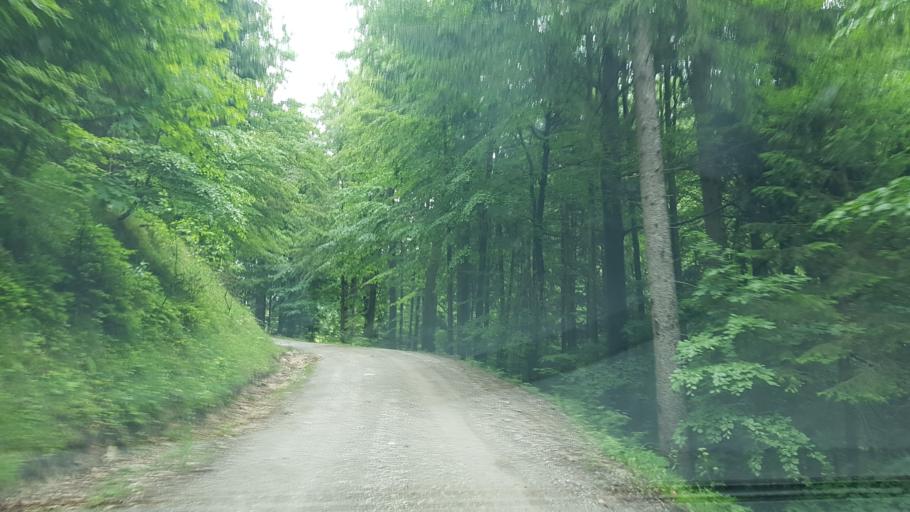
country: SI
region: Dobrna
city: Dobrna
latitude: 46.3844
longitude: 15.2188
